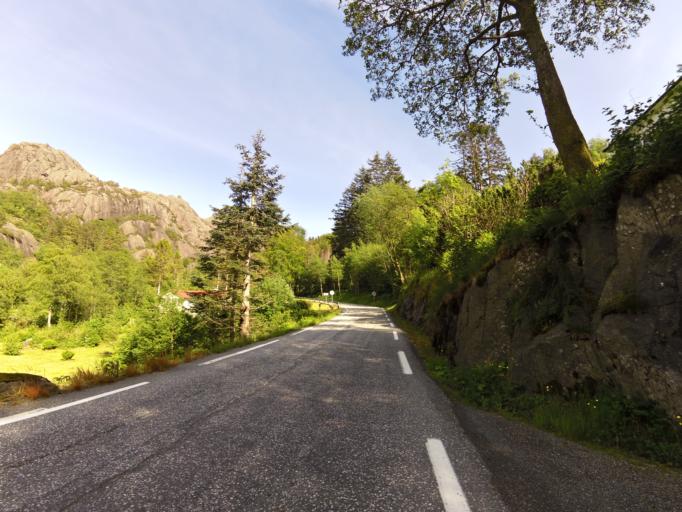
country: NO
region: Rogaland
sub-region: Sokndal
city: Hauge i Dalane
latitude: 58.3155
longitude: 6.3451
